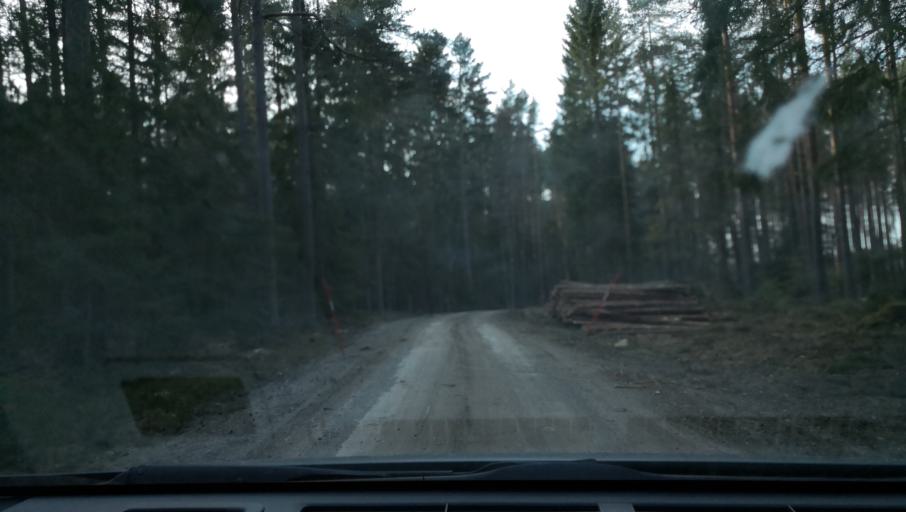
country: SE
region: OErebro
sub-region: Lindesbergs Kommun
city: Frovi
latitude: 59.3554
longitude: 15.3361
